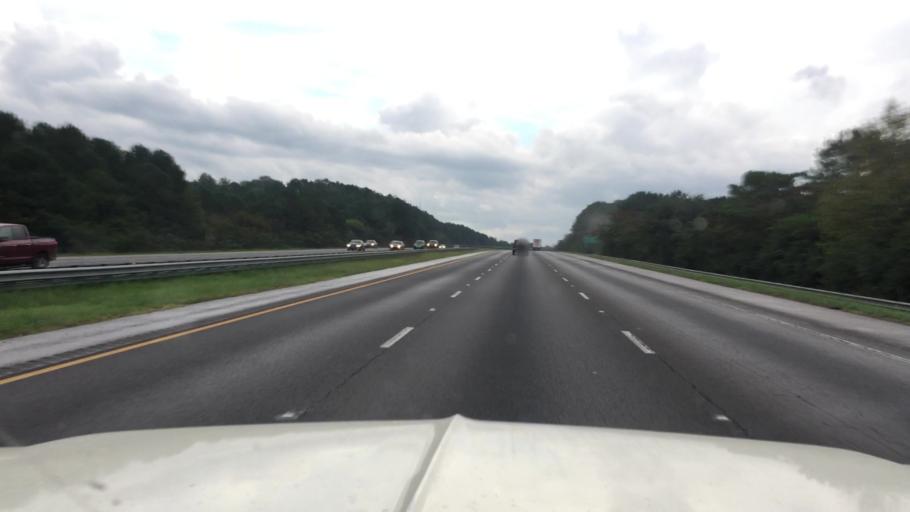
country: US
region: Alabama
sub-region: Jefferson County
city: Mount Olive
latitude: 33.6898
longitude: -86.8313
